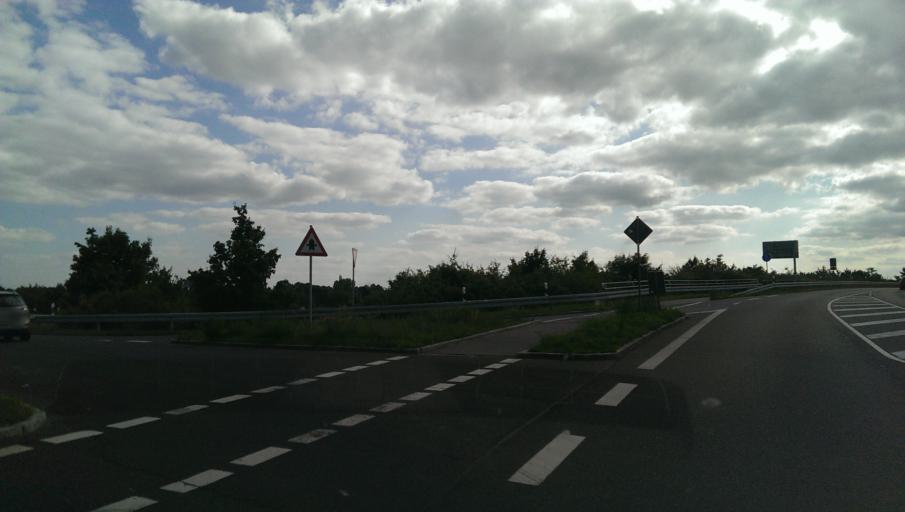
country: DE
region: Saxony-Anhalt
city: Grafenhainichen
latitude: 51.7372
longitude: 12.4811
